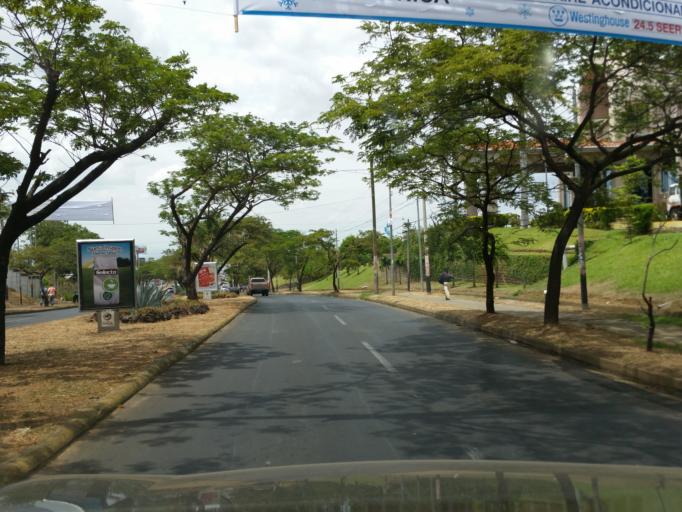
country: NI
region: Managua
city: Managua
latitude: 12.1038
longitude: -86.2532
